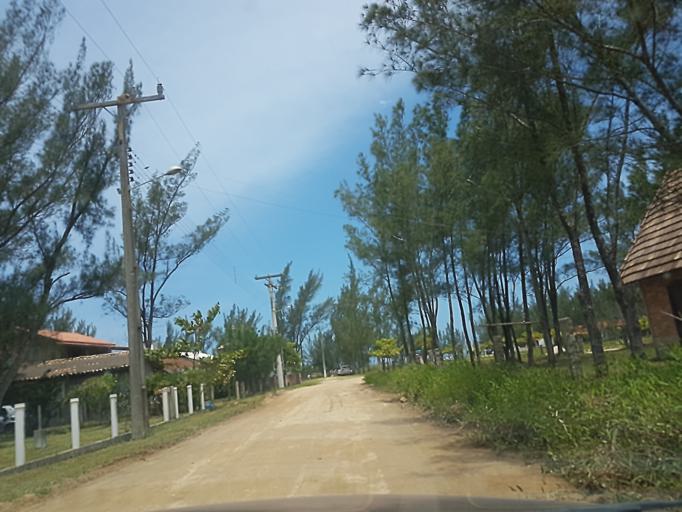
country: BR
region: Santa Catarina
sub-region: Jaguaruna
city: Jaguaruna
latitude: -28.6614
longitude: -48.9605
